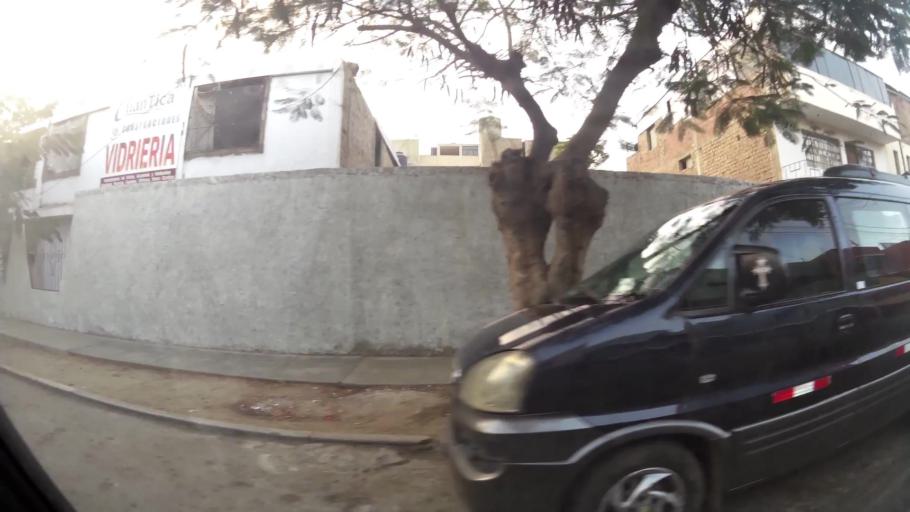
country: PE
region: La Libertad
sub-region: Provincia de Trujillo
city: Trujillo
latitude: -8.1028
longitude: -79.0363
